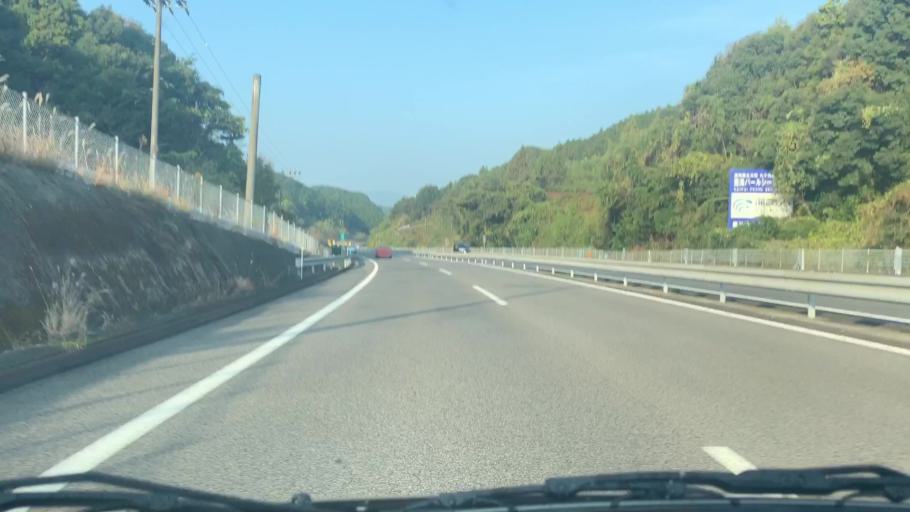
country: JP
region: Saga Prefecture
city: Ureshinomachi-shimojuku
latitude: 33.1545
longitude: 129.9305
